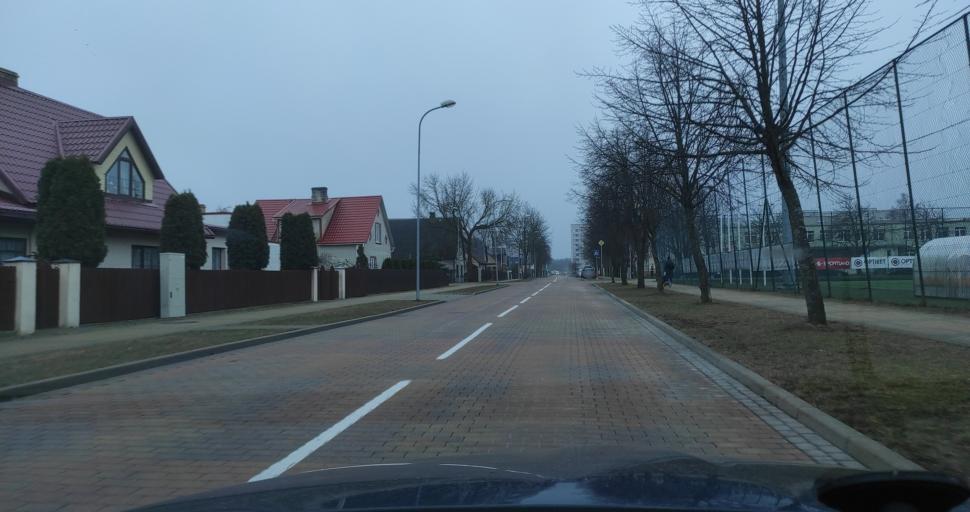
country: LV
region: Ventspils
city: Ventspils
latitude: 57.3874
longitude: 21.5528
